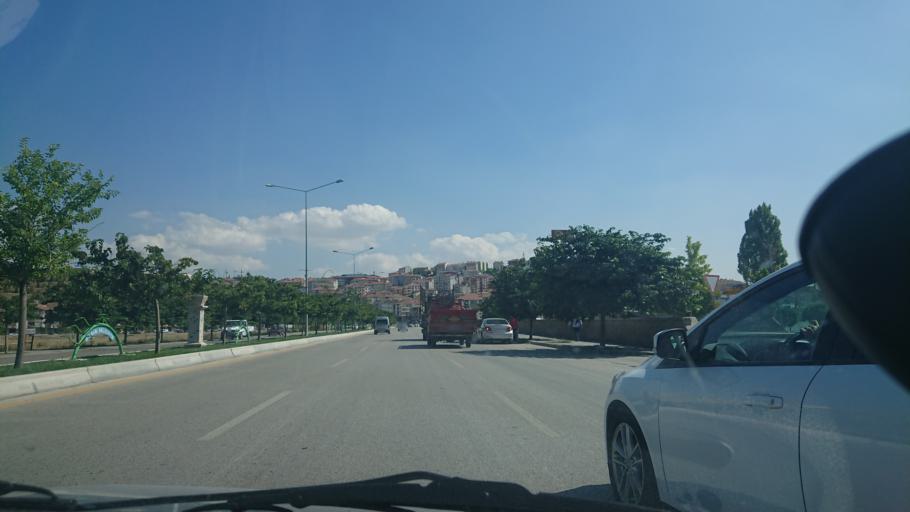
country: TR
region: Ankara
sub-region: Goelbasi
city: Golbasi
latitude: 39.8026
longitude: 32.8093
